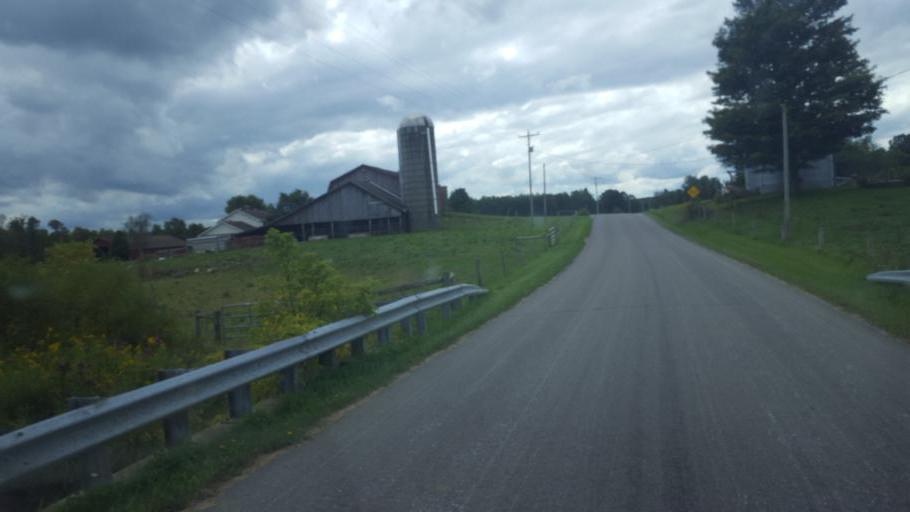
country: US
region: Pennsylvania
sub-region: Crawford County
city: Conneaut Lakeshore
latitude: 41.5077
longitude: -80.2546
